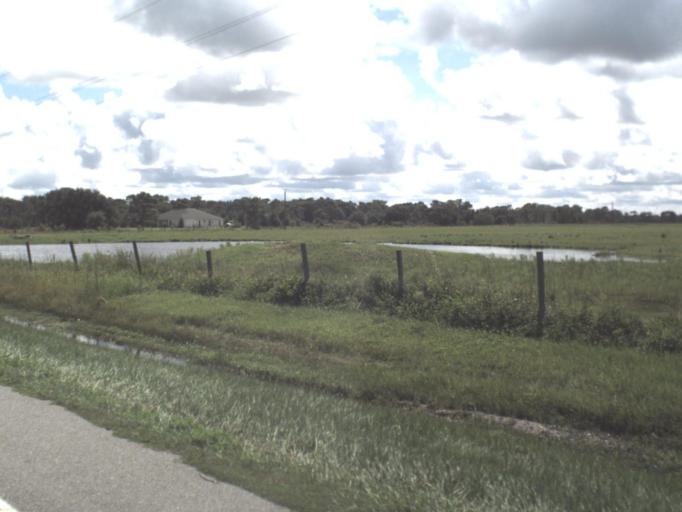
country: US
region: Florida
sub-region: Sarasota County
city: Lake Sarasota
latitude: 27.3641
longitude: -82.2043
